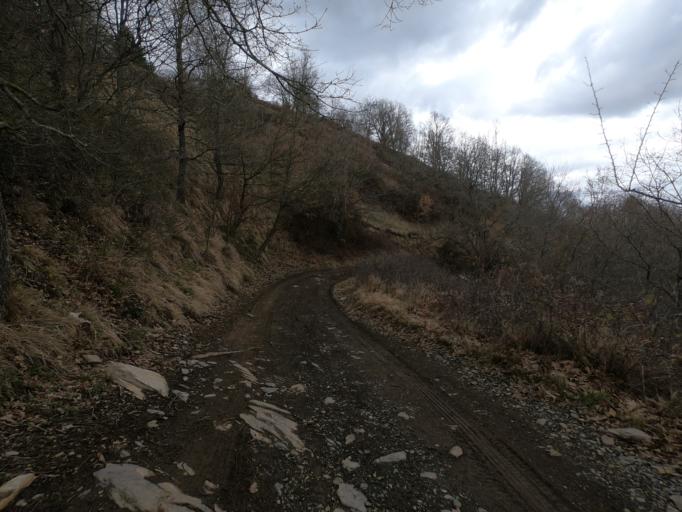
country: IT
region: Liguria
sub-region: Provincia di Imperia
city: Badalucco
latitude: 43.9147
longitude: 7.8790
